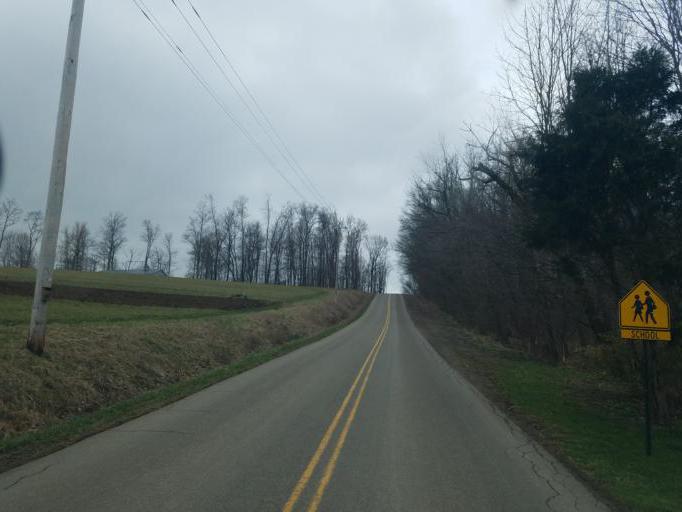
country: US
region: Ohio
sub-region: Knox County
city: Danville
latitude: 40.5234
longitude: -82.3613
